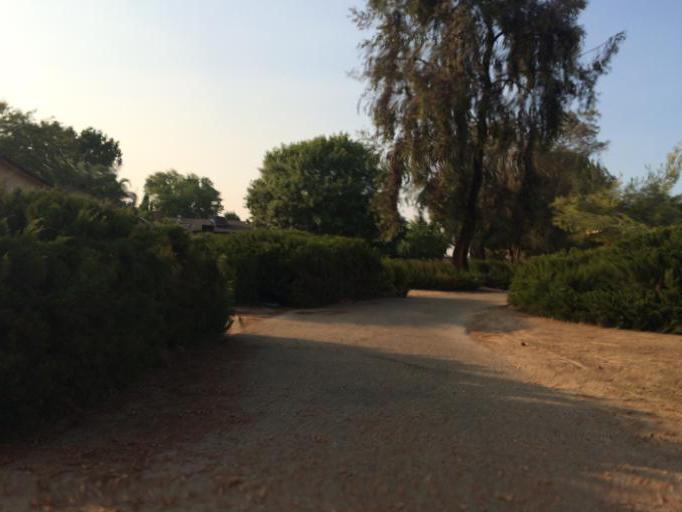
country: US
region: California
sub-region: Fresno County
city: Fresno
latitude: 36.8441
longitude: -119.8107
